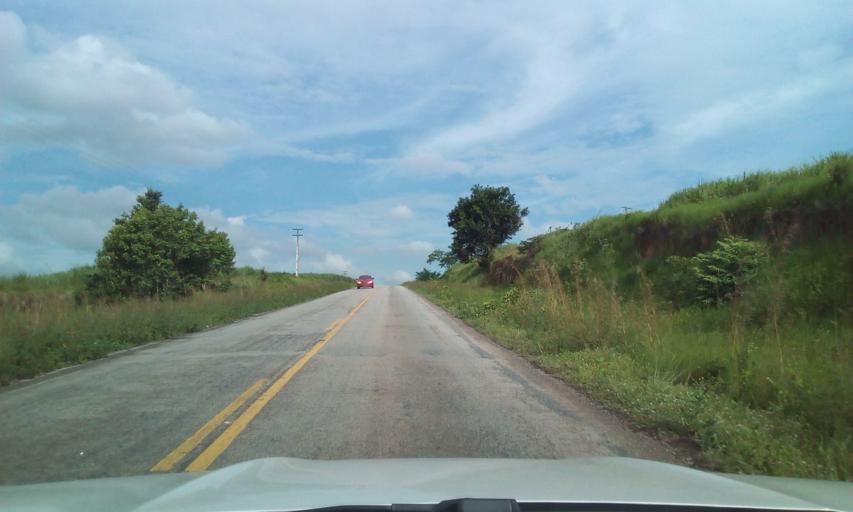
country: BR
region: Paraiba
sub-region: Santa Rita
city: Santa Rita
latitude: -7.0023
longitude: -34.9850
